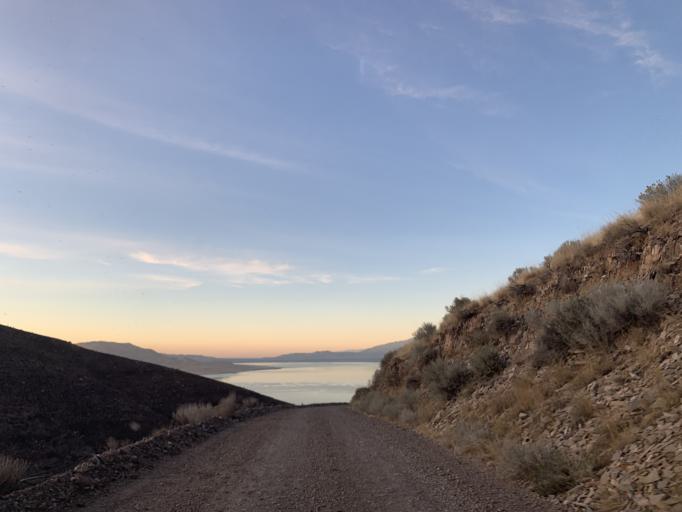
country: US
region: Utah
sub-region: Utah County
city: West Mountain
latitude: 40.0989
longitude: -111.8245
